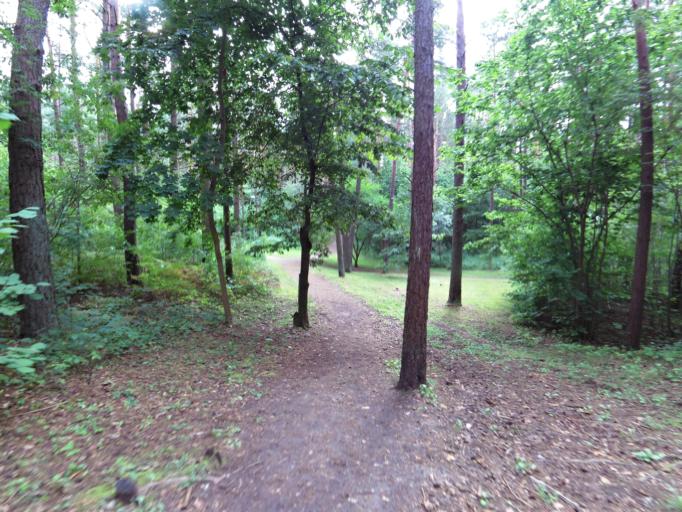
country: LT
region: Vilnius County
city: Lazdynai
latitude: 54.6814
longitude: 25.2003
